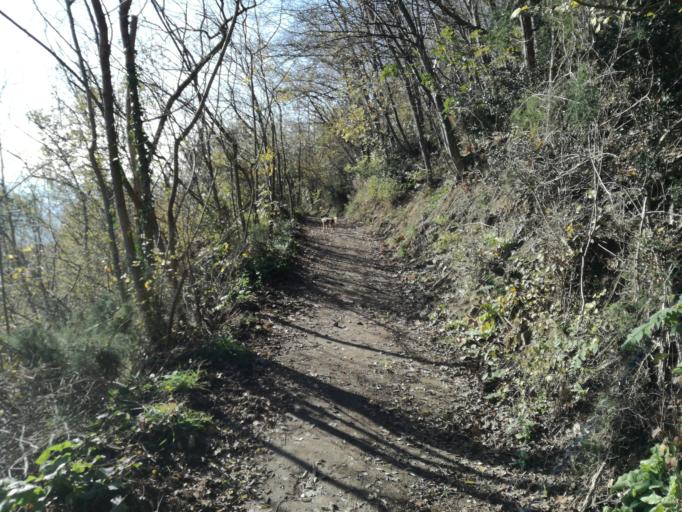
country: IT
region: Veneto
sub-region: Provincia di Padova
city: Arqua Petrarca
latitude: 45.2767
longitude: 11.7298
